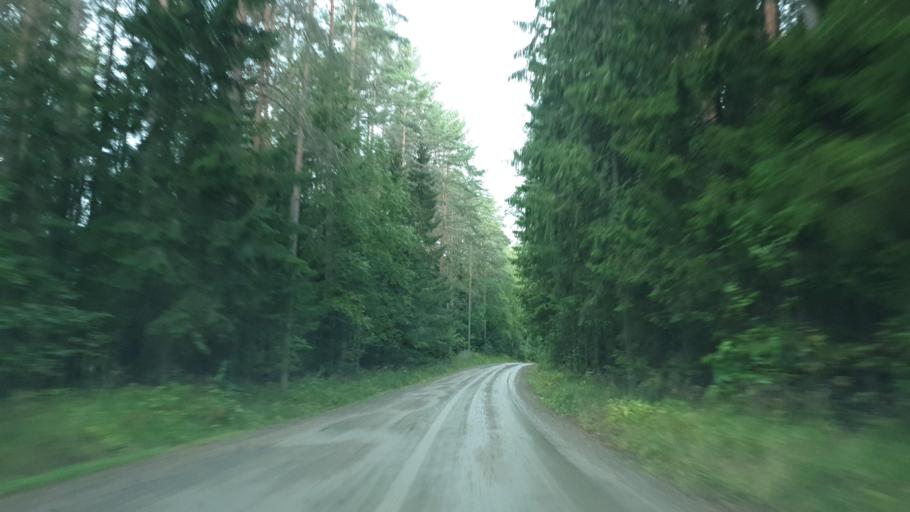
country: FI
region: Northern Savo
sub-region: Kuopio
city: Nilsiae
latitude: 63.1522
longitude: 28.2026
